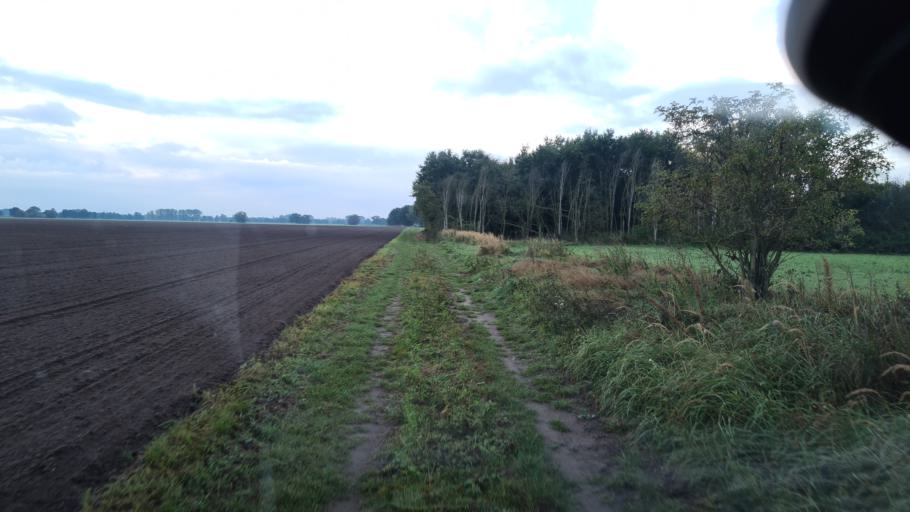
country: DE
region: Brandenburg
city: Schonewalde
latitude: 51.6861
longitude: 13.5697
